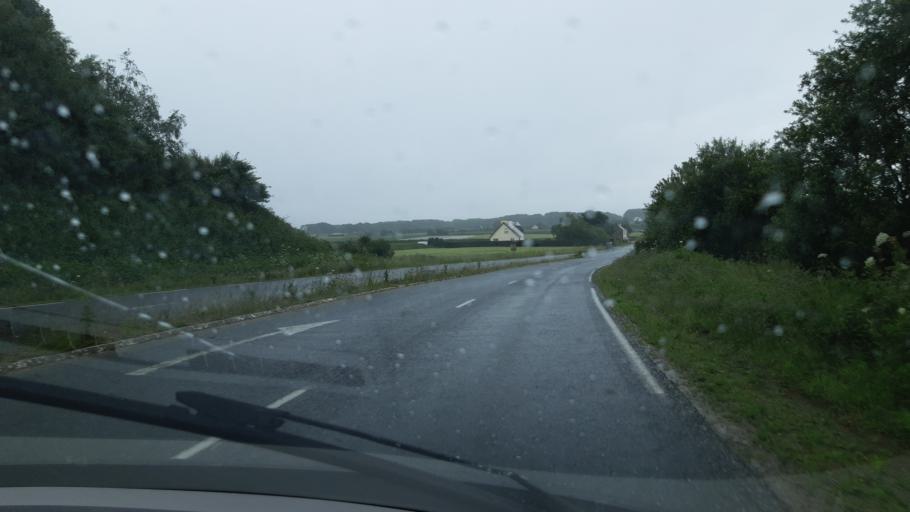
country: FR
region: Brittany
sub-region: Departement du Finistere
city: Plouvorn
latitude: 48.6012
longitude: -4.0528
